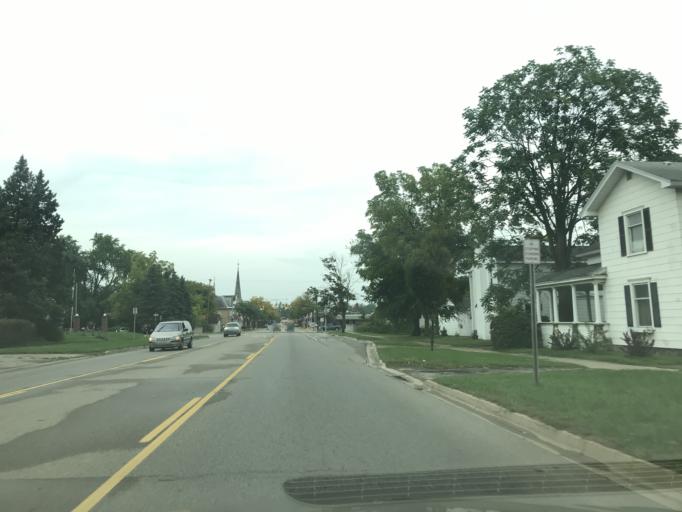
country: US
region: Michigan
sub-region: Eaton County
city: Eaton Rapids
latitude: 42.5080
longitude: -84.6560
